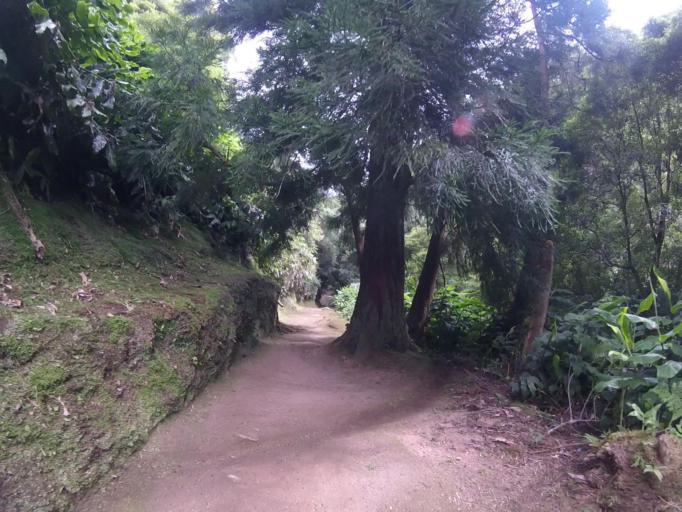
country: PT
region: Azores
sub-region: Vila Franca do Campo
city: Vila Franca do Campo
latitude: 37.7461
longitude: -25.5133
